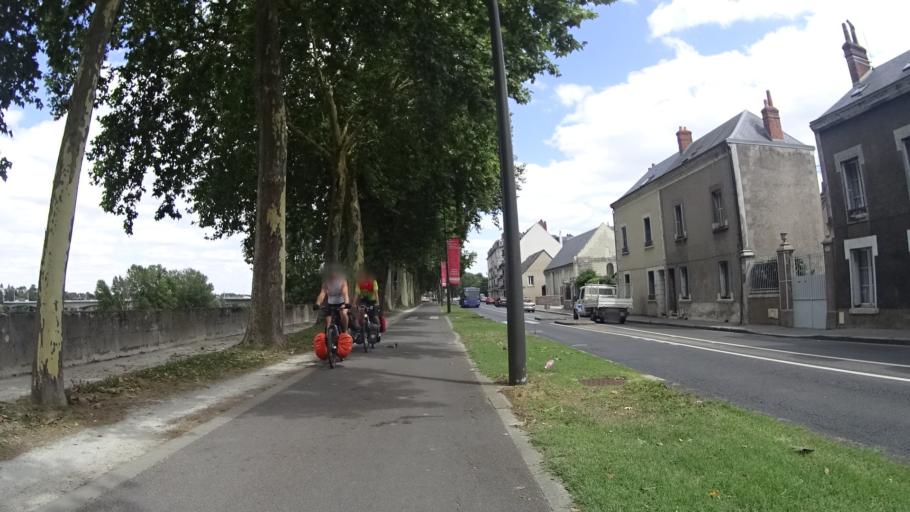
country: FR
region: Centre
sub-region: Departement d'Indre-et-Loire
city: Tours
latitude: 47.3976
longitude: 0.6962
